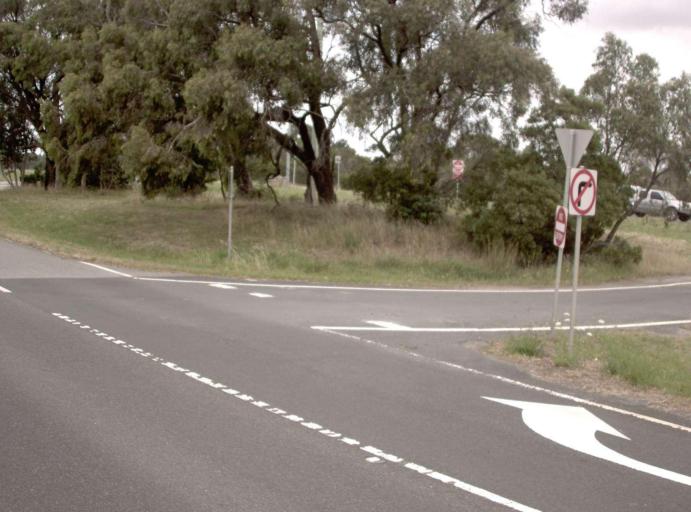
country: AU
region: Victoria
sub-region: Cardinia
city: Pakenham Upper
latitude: -38.0656
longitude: 145.5063
